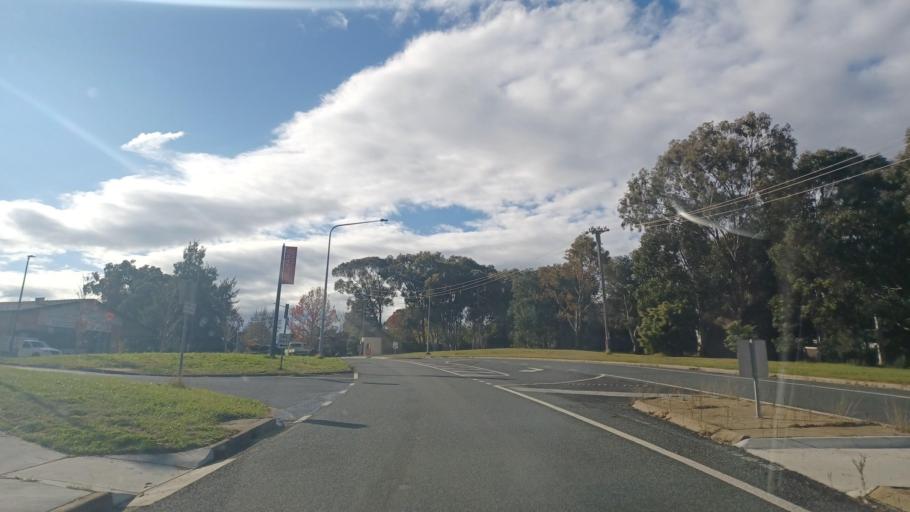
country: AU
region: Australian Capital Territory
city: Belconnen
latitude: -35.1990
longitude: 149.0446
